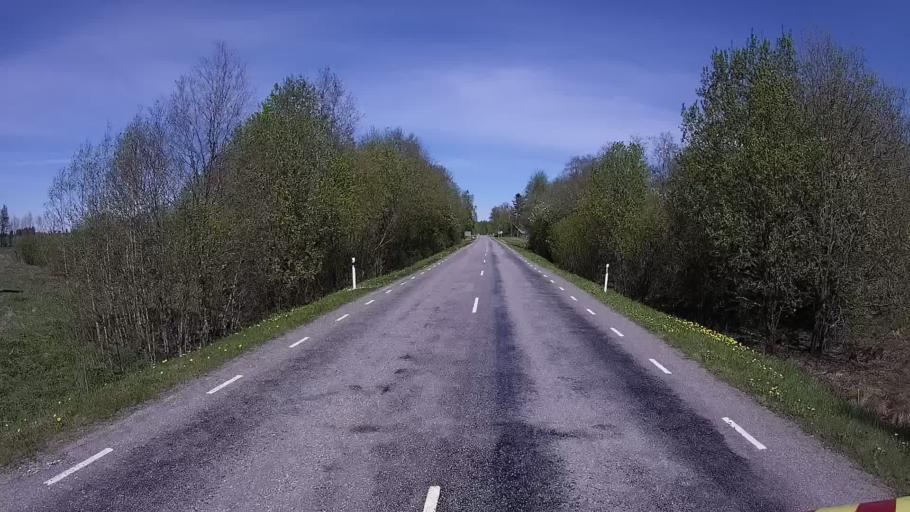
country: EE
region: Harju
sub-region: Rae vald
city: Vaida
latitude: 59.0666
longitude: 25.1547
